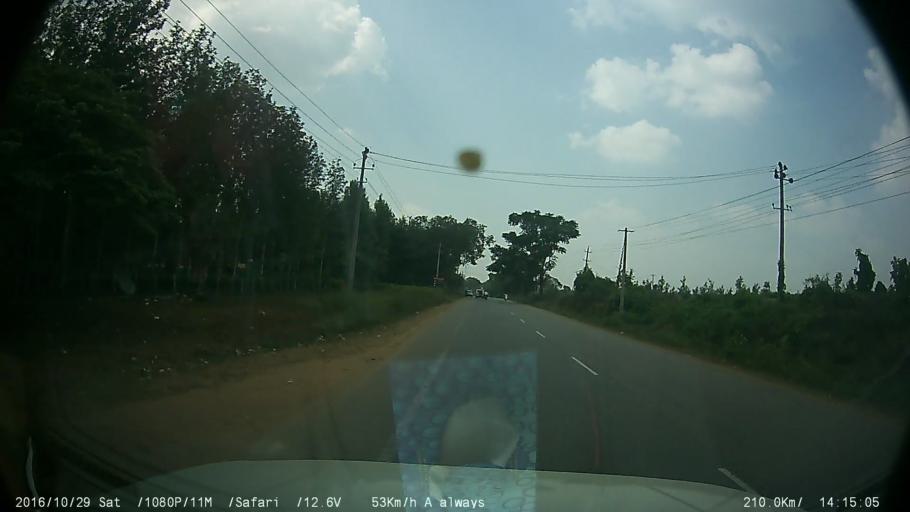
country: IN
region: Karnataka
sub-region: Mysore
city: Piriyapatna
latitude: 12.3824
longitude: 76.0325
